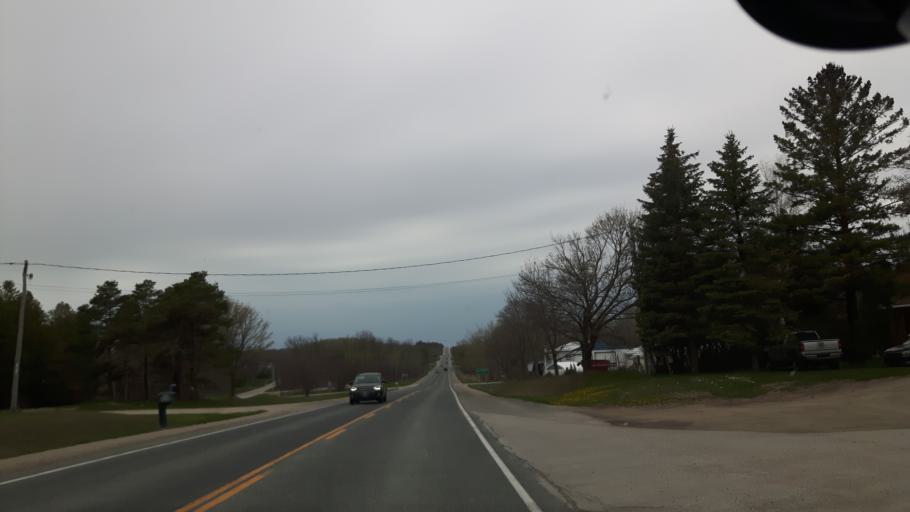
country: CA
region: Ontario
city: Goderich
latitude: 43.6387
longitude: -81.5890
